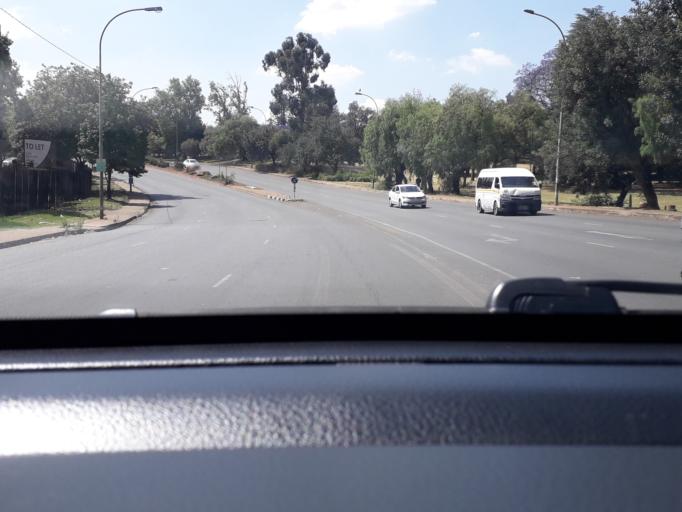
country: ZA
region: Gauteng
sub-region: City of Johannesburg Metropolitan Municipality
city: Johannesburg
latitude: -26.1849
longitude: 28.0410
